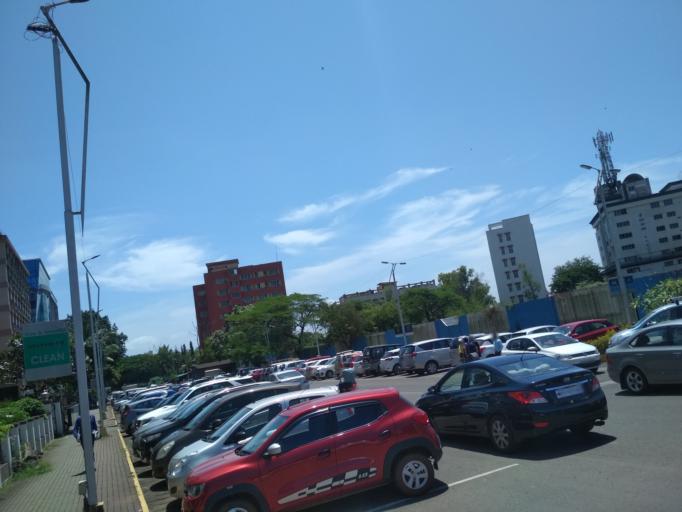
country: IN
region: Goa
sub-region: North Goa
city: Panaji
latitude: 15.4946
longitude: 73.8349
